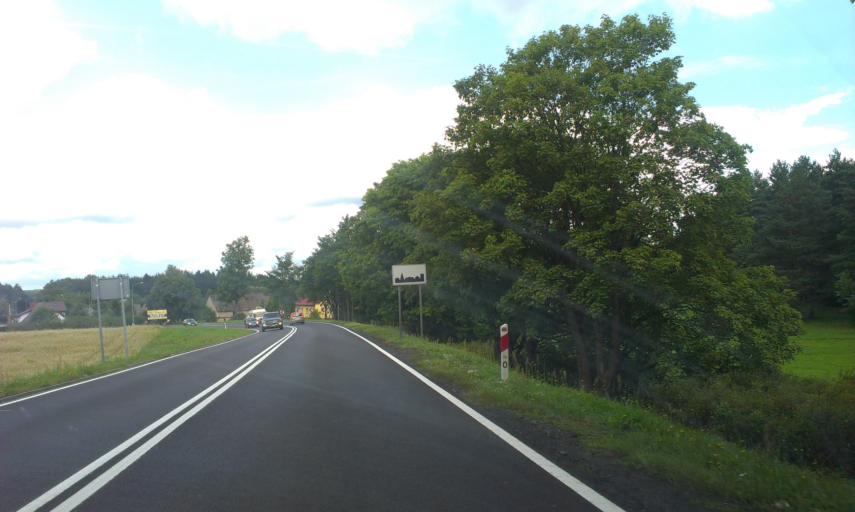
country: PL
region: West Pomeranian Voivodeship
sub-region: Powiat koszalinski
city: Bobolice
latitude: 53.9991
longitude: 16.5250
